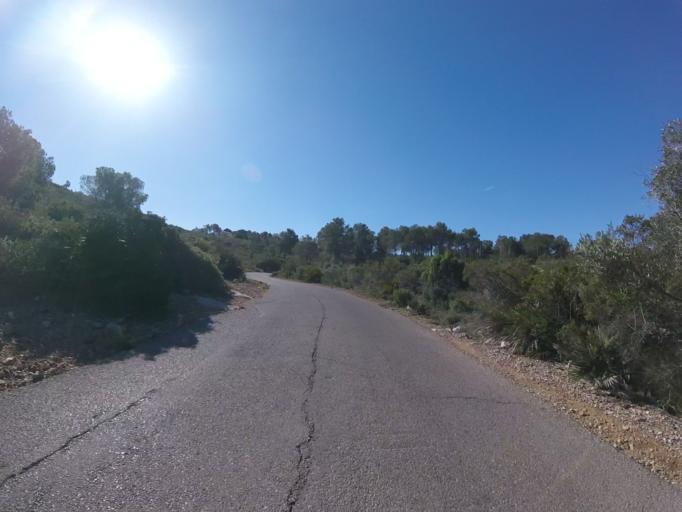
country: ES
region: Valencia
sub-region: Provincia de Castello
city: Orpesa/Oropesa del Mar
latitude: 40.0839
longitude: 0.1242
